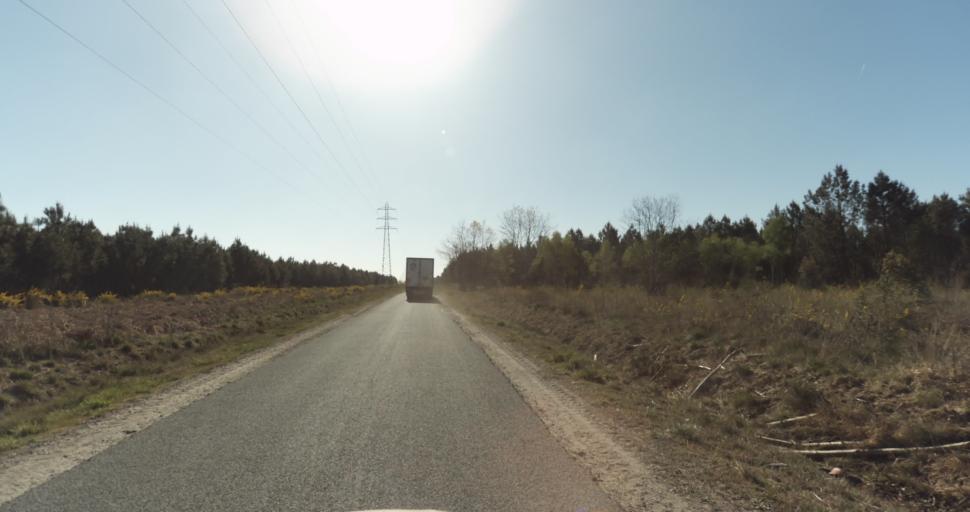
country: FR
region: Aquitaine
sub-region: Departement de la Gironde
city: Marcheprime
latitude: 44.7502
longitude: -0.8467
